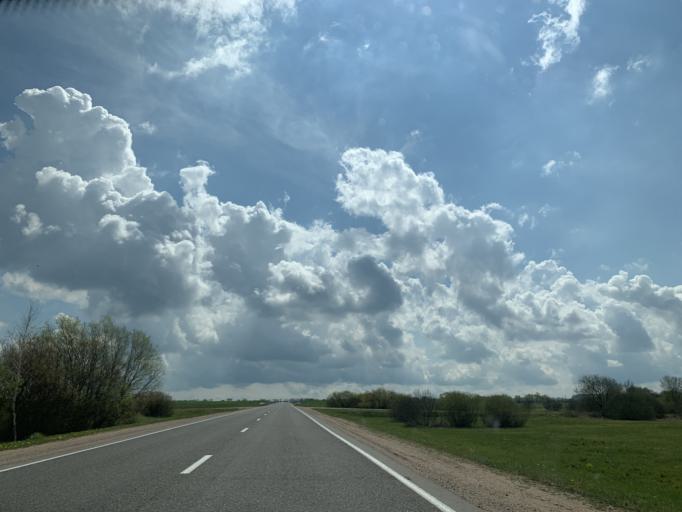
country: BY
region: Minsk
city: Nyasvizh
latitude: 53.2413
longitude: 26.7084
